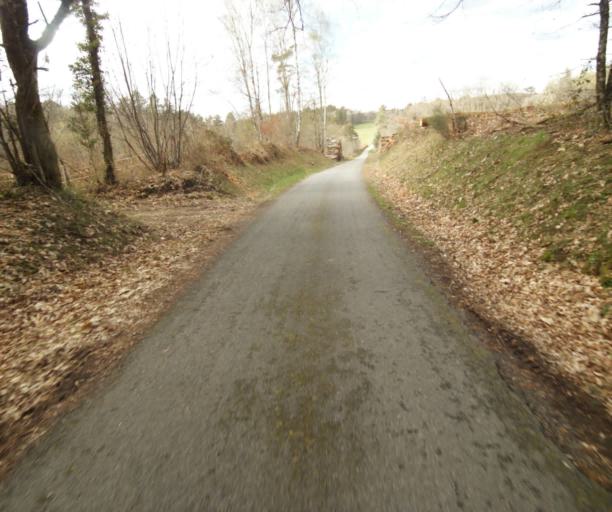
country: FR
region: Limousin
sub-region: Departement de la Correze
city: Argentat
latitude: 45.1927
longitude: 1.9285
